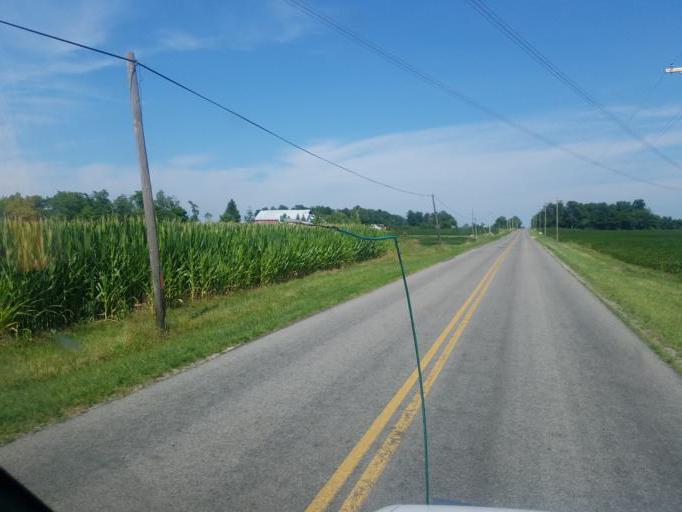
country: US
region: Ohio
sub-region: Shelby County
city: Jackson Center
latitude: 40.4977
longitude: -84.0697
